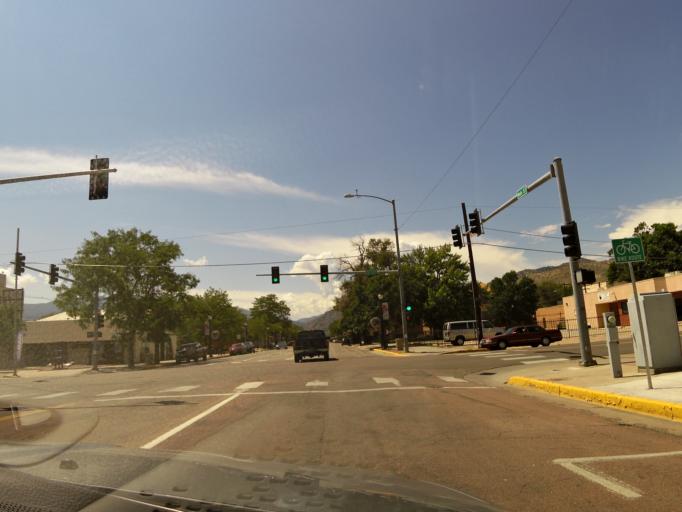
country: US
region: Colorado
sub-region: Fremont County
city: Canon City
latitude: 38.4432
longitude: -105.2353
